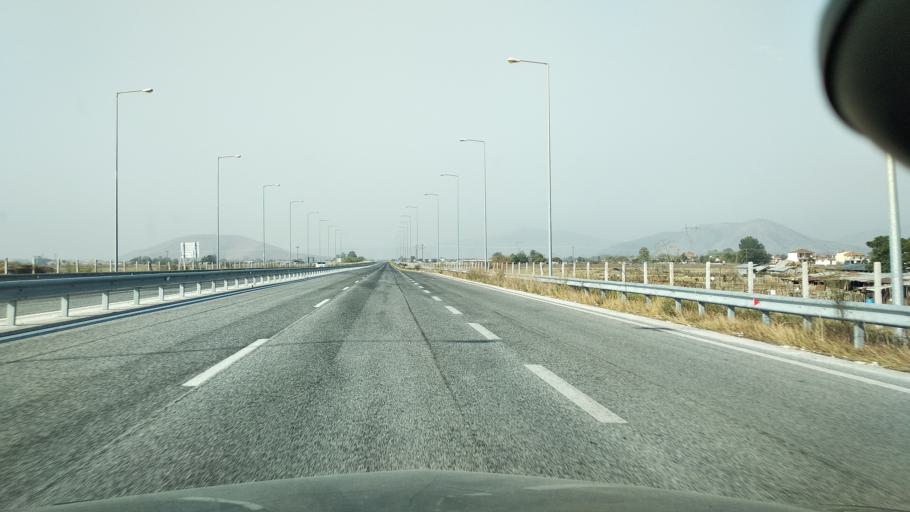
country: GR
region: Thessaly
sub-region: Trikala
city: Farkadona
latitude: 39.5837
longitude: 22.0681
